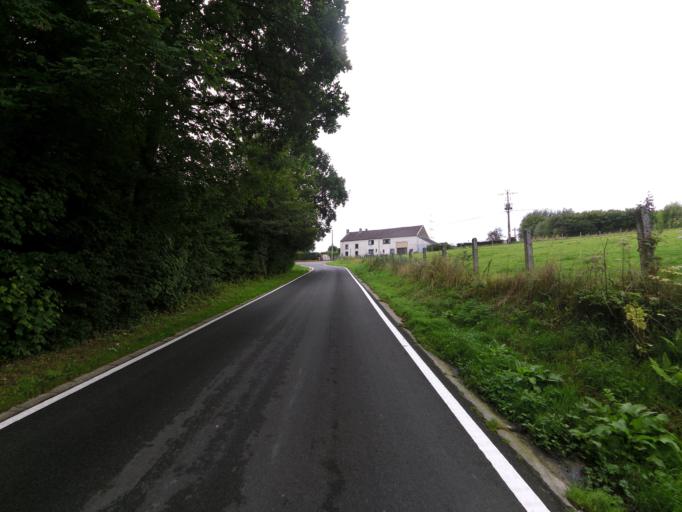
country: BE
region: Wallonia
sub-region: Province de Liege
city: Amay
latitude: 50.5278
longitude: 5.3594
